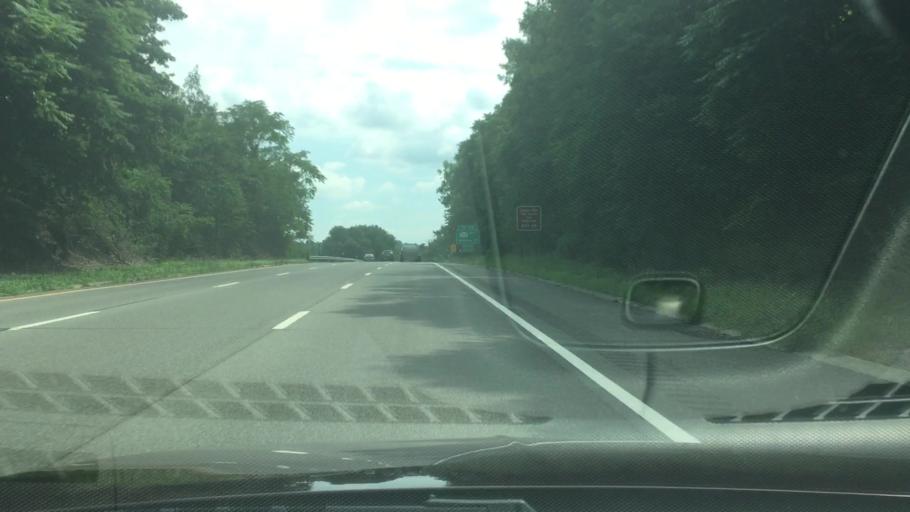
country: US
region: New York
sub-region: Westchester County
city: Yorktown Heights
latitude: 41.2180
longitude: -73.8116
